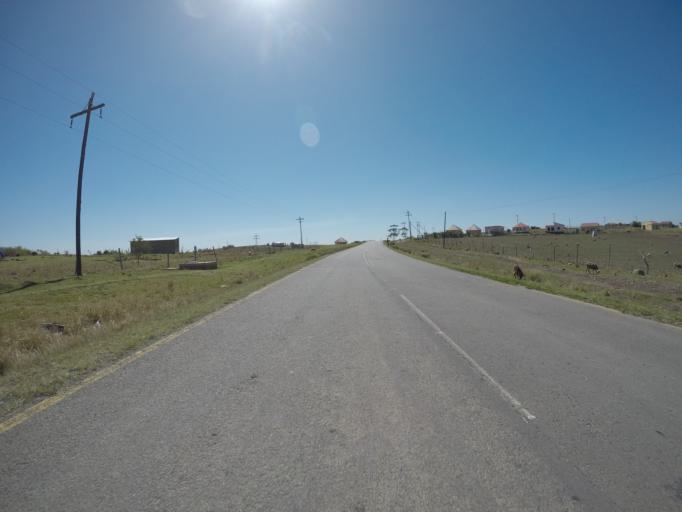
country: ZA
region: Eastern Cape
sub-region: OR Tambo District Municipality
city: Libode
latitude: -31.9082
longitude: 29.0004
